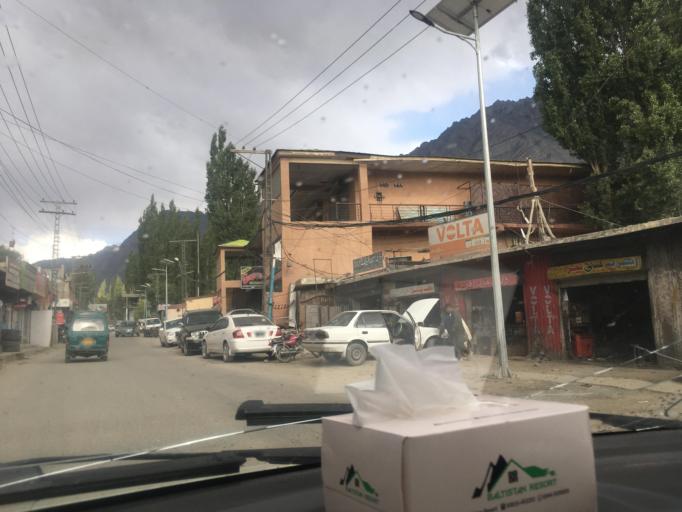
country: PK
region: Gilgit-Baltistan
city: Skardu
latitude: 35.2976
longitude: 75.6408
